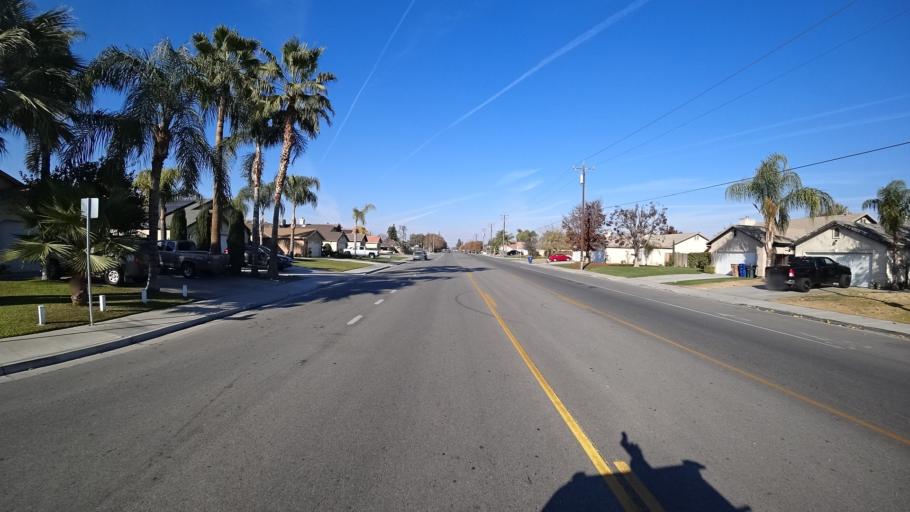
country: US
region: California
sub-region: Kern County
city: Greenfield
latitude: 35.2910
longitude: -119.0478
